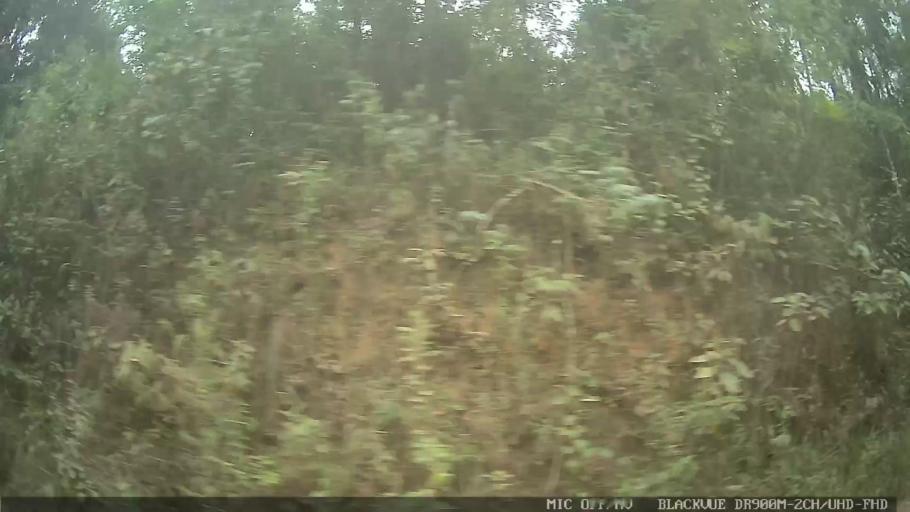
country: BR
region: Sao Paulo
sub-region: Bom Jesus Dos Perdoes
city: Bom Jesus dos Perdoes
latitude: -23.1606
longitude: -46.5100
